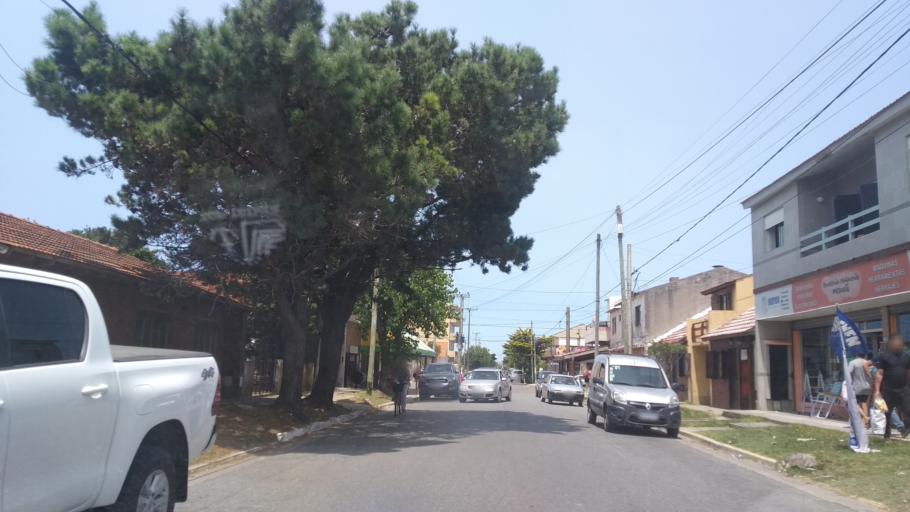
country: AR
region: Buenos Aires
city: Mar del Tuyu
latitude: -36.5584
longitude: -56.6895
